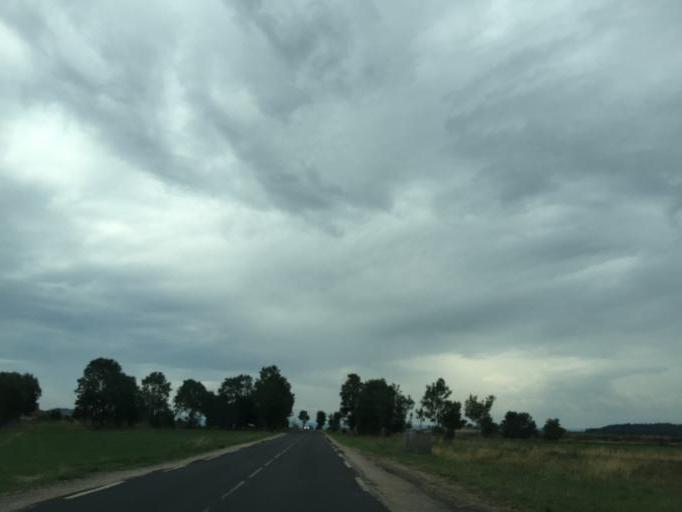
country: FR
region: Auvergne
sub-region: Departement de la Haute-Loire
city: Solignac-sur-Loire
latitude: 44.8573
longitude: 3.8436
